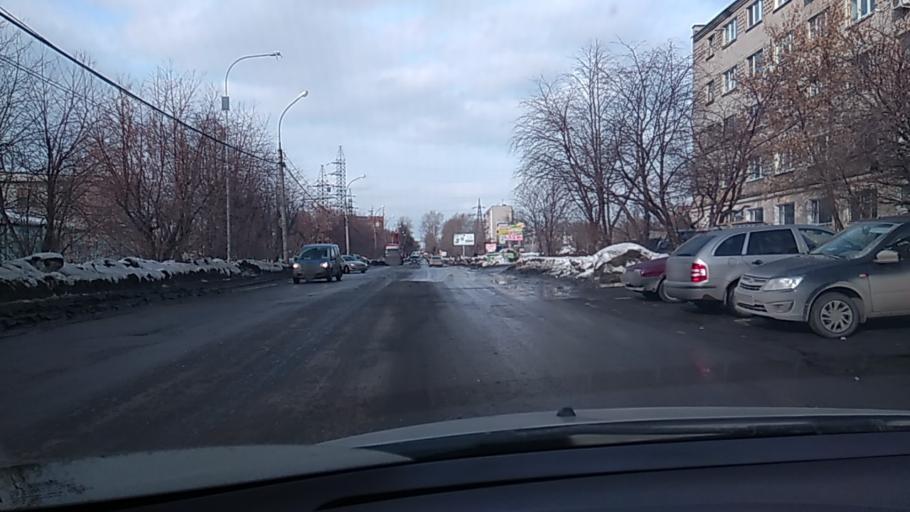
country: RU
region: Sverdlovsk
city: Yekaterinburg
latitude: 56.8656
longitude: 60.6529
